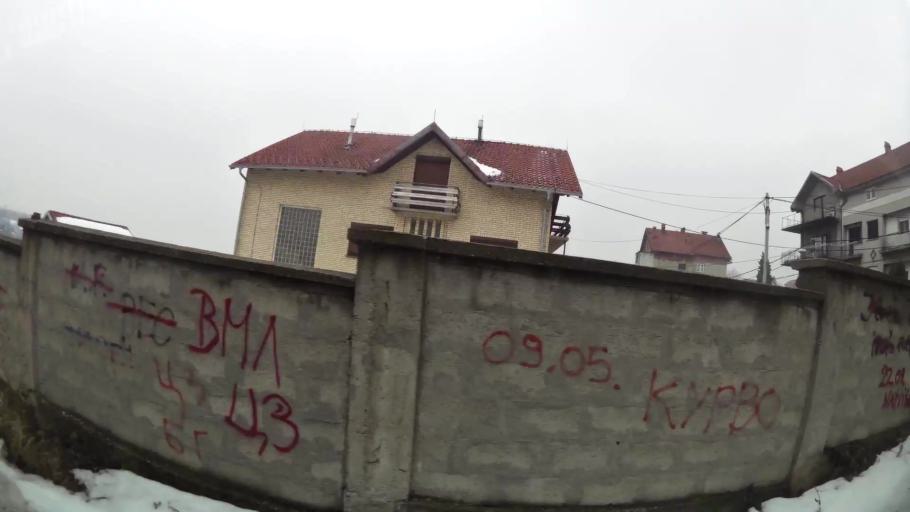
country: RS
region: Central Serbia
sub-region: Belgrade
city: Zvezdara
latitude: 44.7574
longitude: 20.5252
